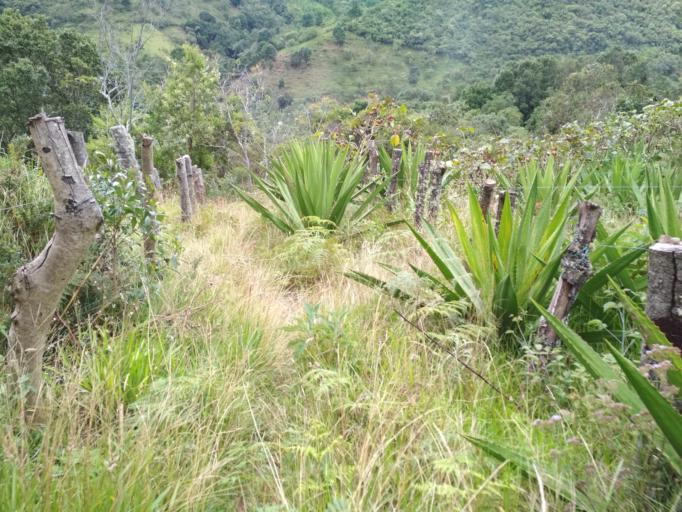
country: CO
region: Cauca
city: Totoro
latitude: 2.5316
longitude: -76.4220
